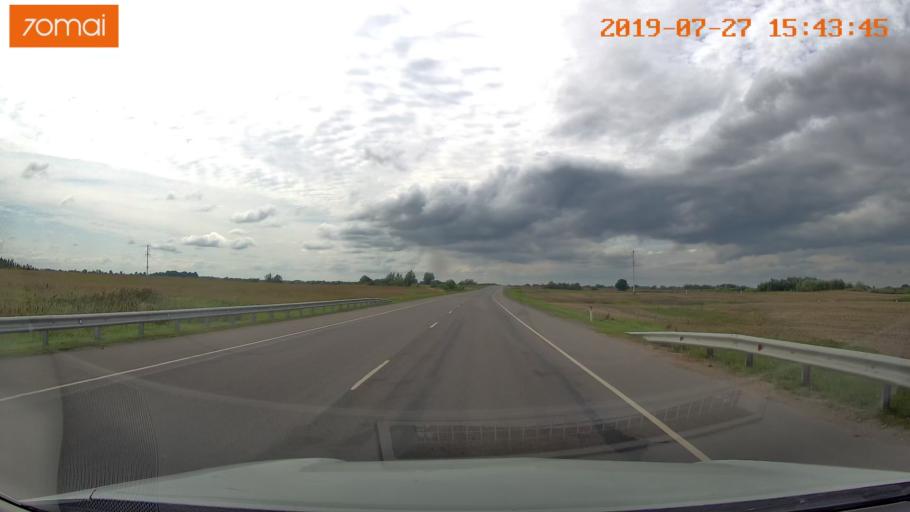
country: RU
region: Kaliningrad
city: Gusev
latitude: 54.6148
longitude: 22.1844
